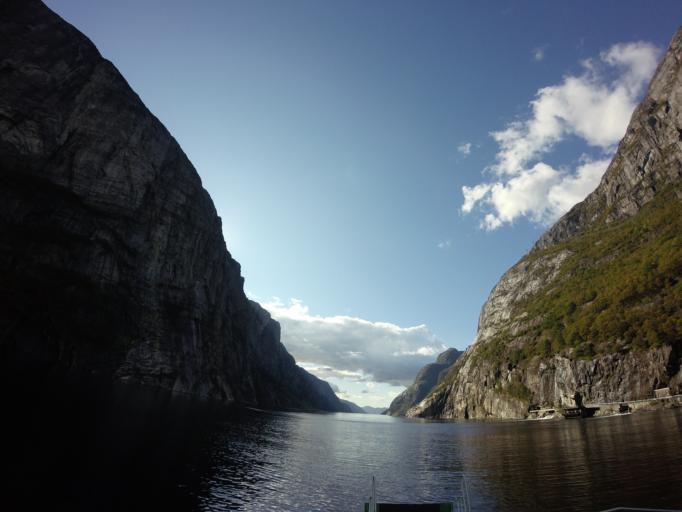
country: NO
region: Vest-Agder
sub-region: Sirdal
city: Tonstad
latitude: 59.0502
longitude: 6.6218
